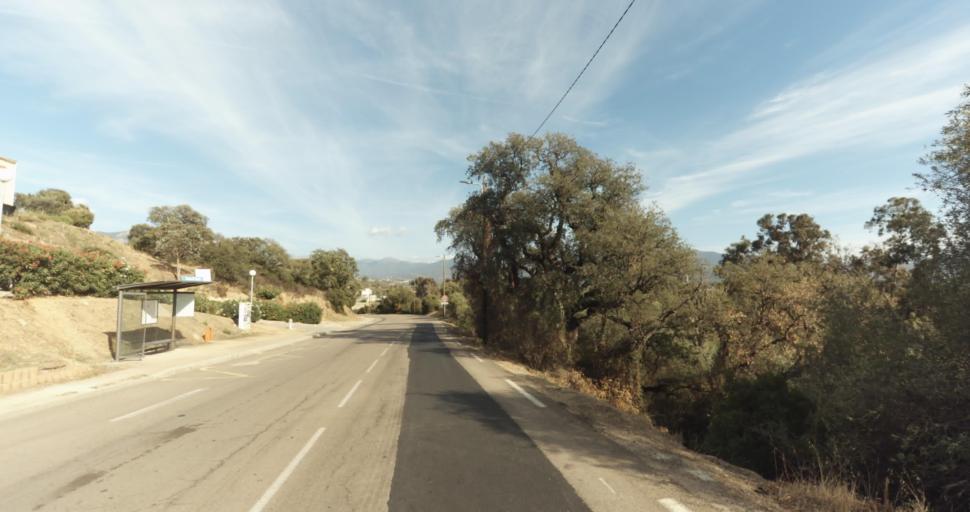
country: FR
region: Corsica
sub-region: Departement de la Corse-du-Sud
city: Ajaccio
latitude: 41.9299
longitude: 8.7809
